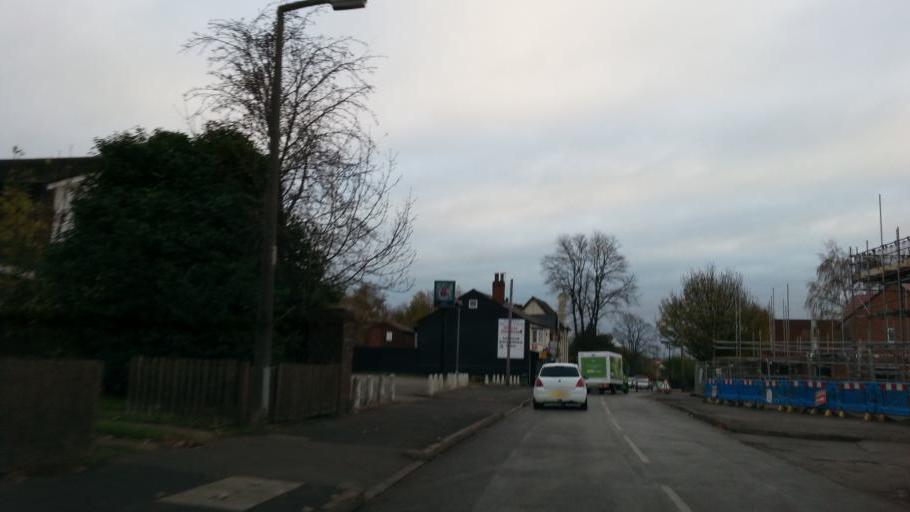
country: GB
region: England
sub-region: Sandwell
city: Wednesbury
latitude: 52.5429
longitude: -2.0426
